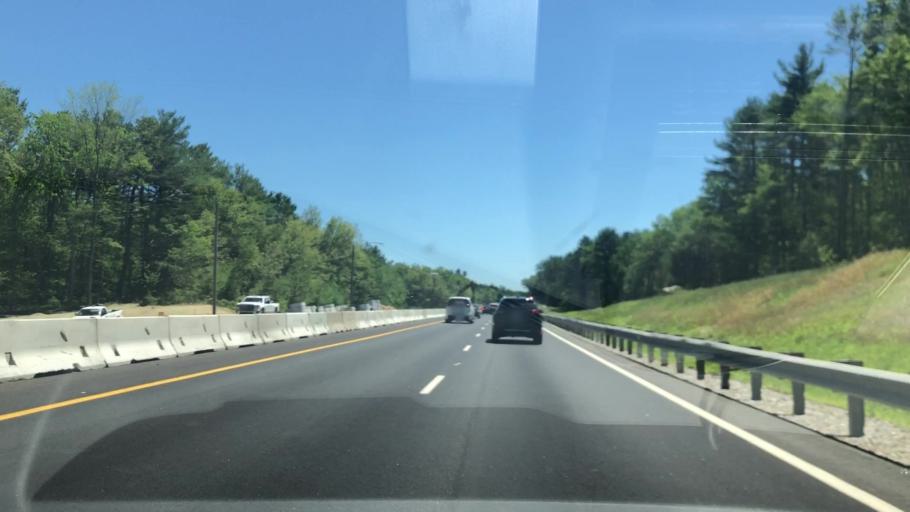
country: US
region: New Hampshire
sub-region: Rockingham County
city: Auburn
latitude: 42.9470
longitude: -71.3954
